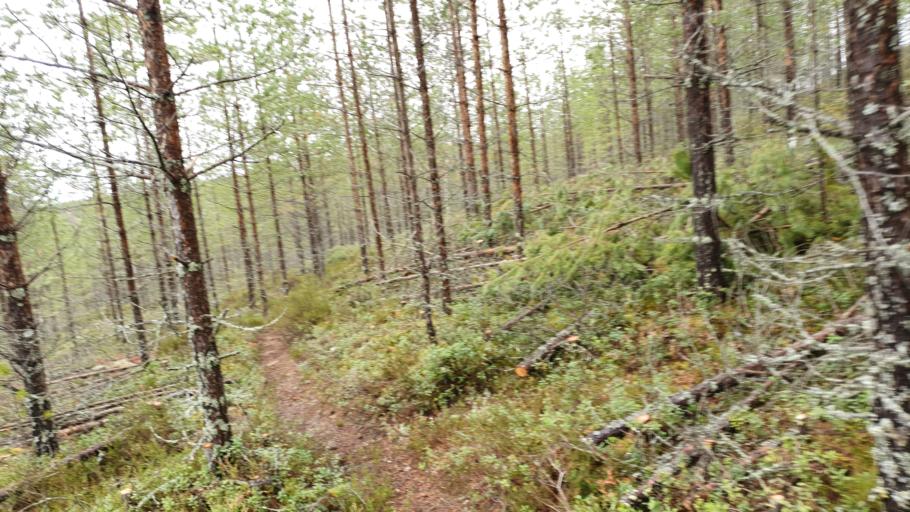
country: FI
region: Kainuu
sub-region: Kehys-Kainuu
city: Kuhmo
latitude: 64.1506
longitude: 29.3997
